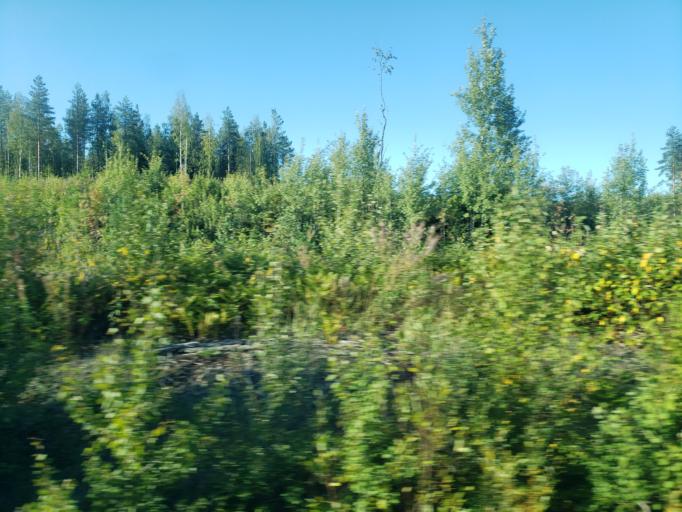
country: FI
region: South Karelia
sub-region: Lappeenranta
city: Ylaemaa
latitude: 60.9332
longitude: 27.9355
